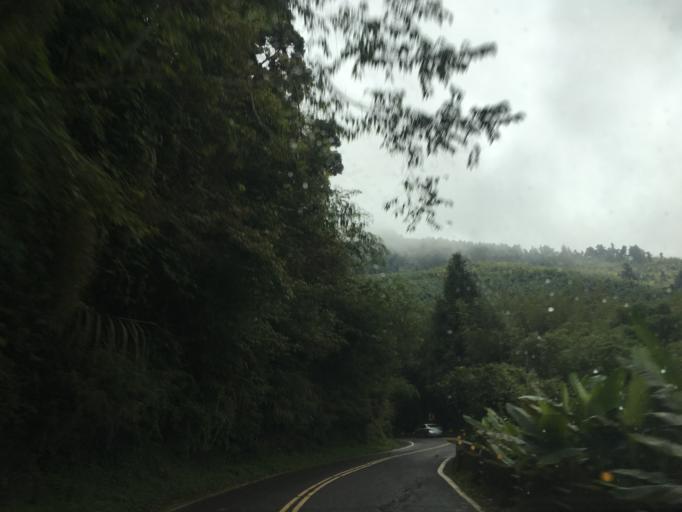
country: TW
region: Taiwan
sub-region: Chiayi
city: Jiayi Shi
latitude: 23.4876
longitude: 120.6990
